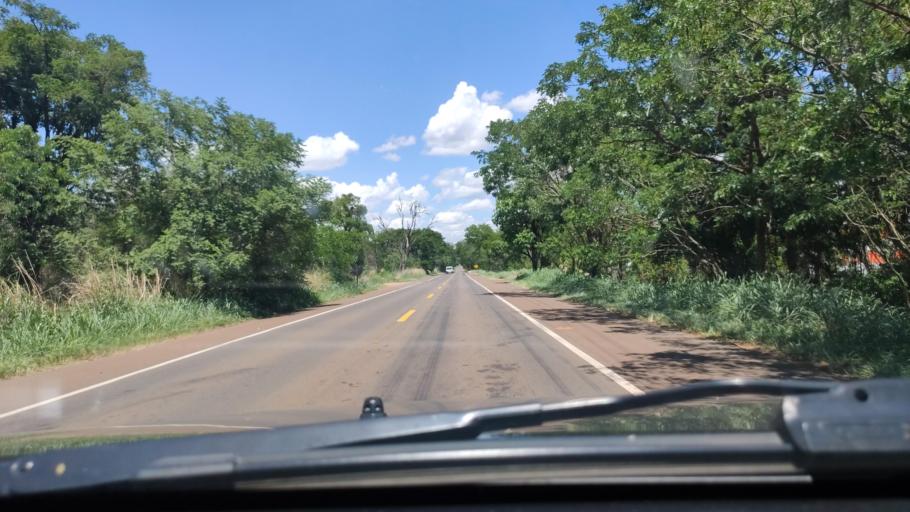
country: BR
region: Sao Paulo
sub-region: Boa Esperanca Do Sul
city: Boa Esperanca do Sul
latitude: -22.0690
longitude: -48.3733
